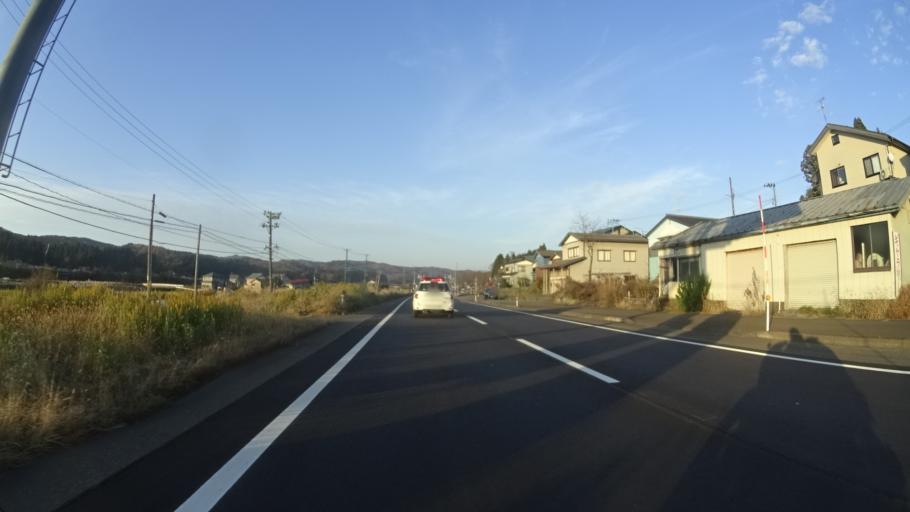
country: JP
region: Niigata
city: Nagaoka
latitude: 37.4433
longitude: 138.7426
